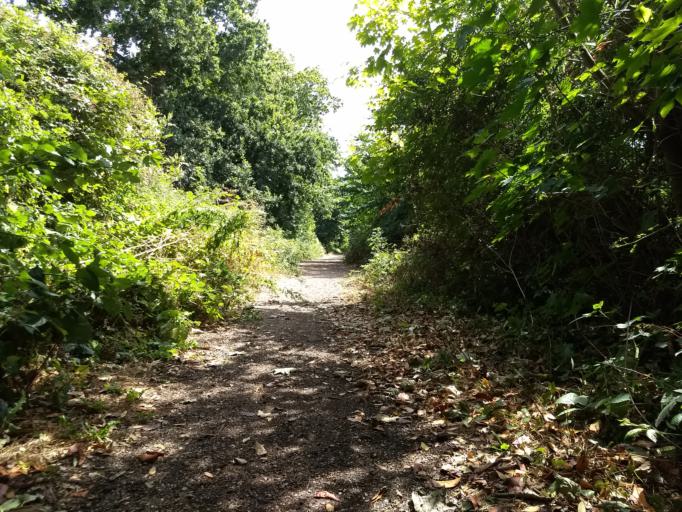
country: GB
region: England
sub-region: Isle of Wight
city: Gurnard
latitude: 50.7607
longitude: -1.3190
